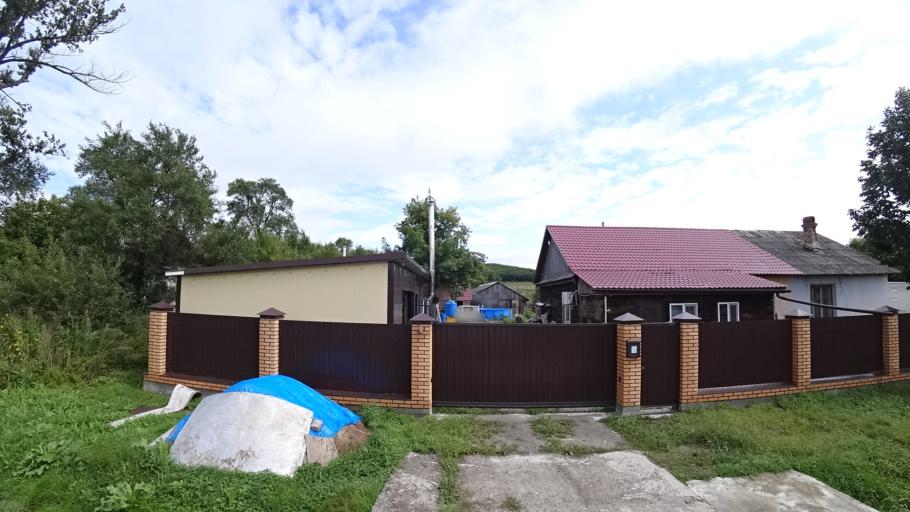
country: RU
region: Primorskiy
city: Lyalichi
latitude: 44.1362
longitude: 132.3728
